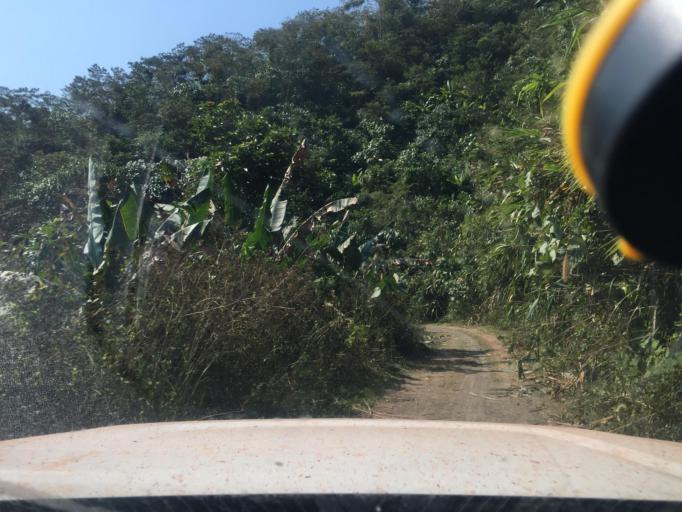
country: LA
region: Phongsali
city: Phongsali
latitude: 21.6873
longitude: 102.4090
